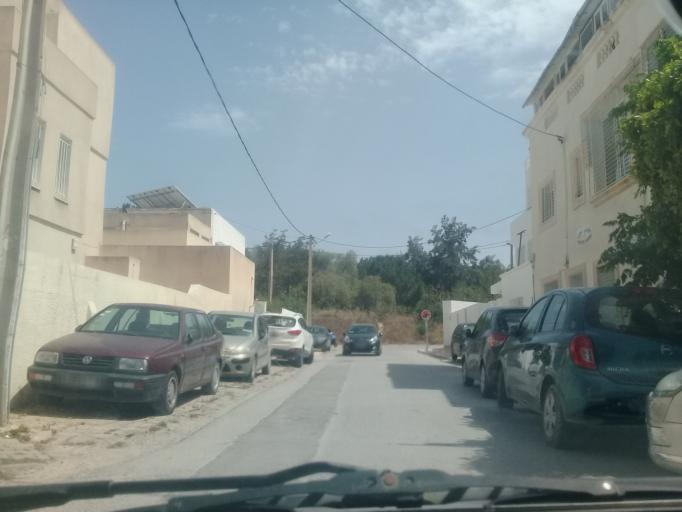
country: TN
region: Tunis
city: Al Marsa
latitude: 36.8766
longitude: 10.3315
